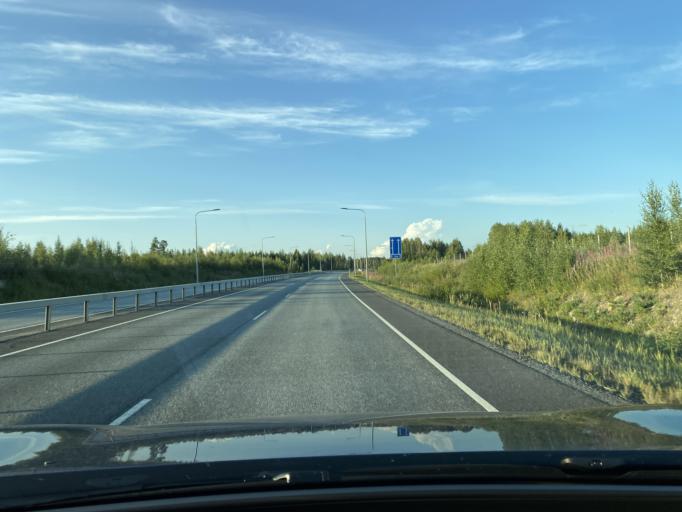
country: FI
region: Southern Ostrobothnia
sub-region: Seinaejoki
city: Seinaejoki
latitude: 62.6994
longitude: 22.8173
